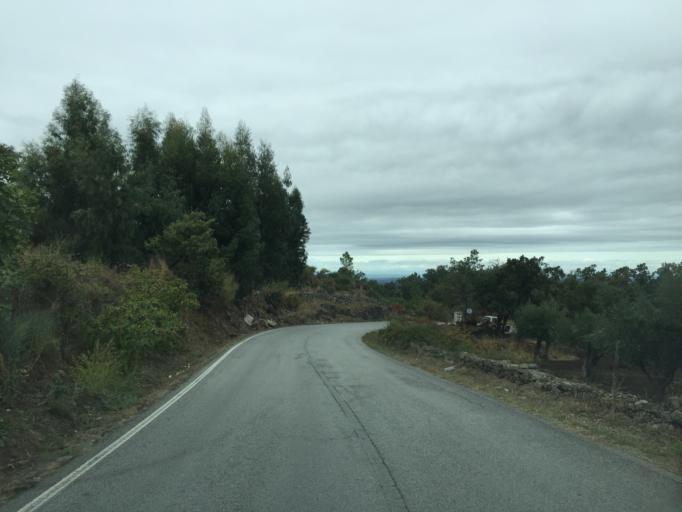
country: PT
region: Portalegre
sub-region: Marvao
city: Marvao
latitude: 39.4014
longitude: -7.3708
